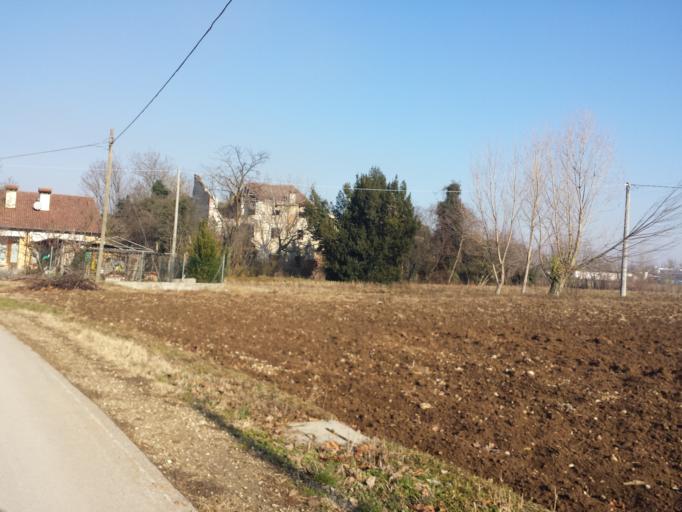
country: IT
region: Veneto
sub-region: Provincia di Vicenza
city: Sandrigo
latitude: 45.6433
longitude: 11.6015
